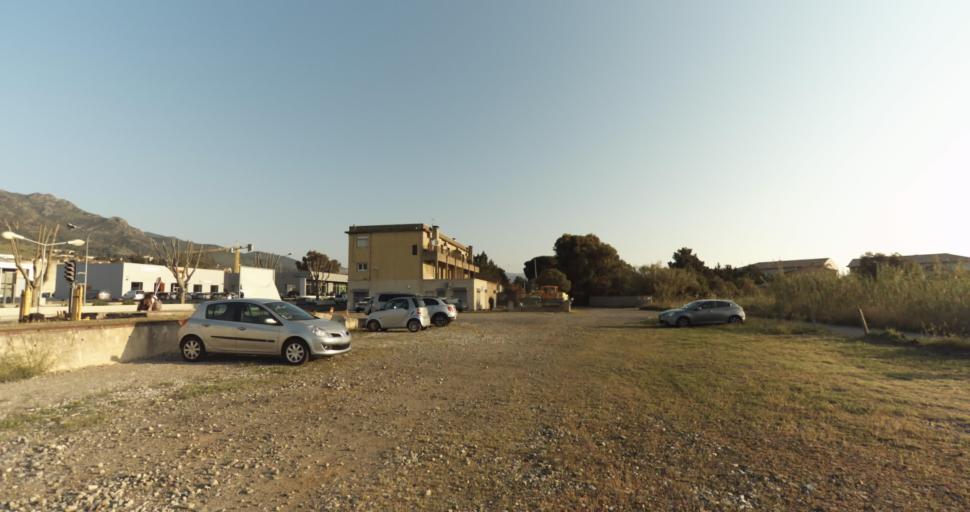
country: FR
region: Corsica
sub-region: Departement de la Haute-Corse
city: Biguglia
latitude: 42.6151
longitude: 9.4380
